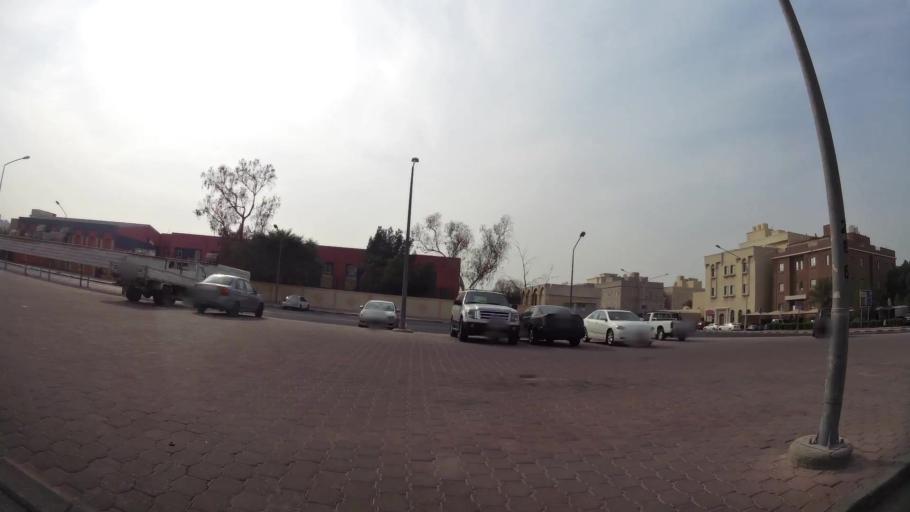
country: KW
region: Al Farwaniyah
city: Al Farwaniyah
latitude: 29.2940
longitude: 47.9625
